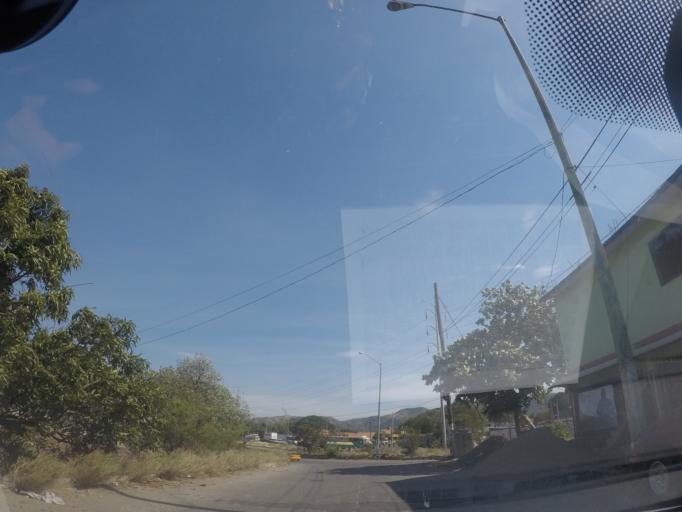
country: MX
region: Oaxaca
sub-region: Santo Domingo Tehuantepec
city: La Noria
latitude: 16.2231
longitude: -95.2092
